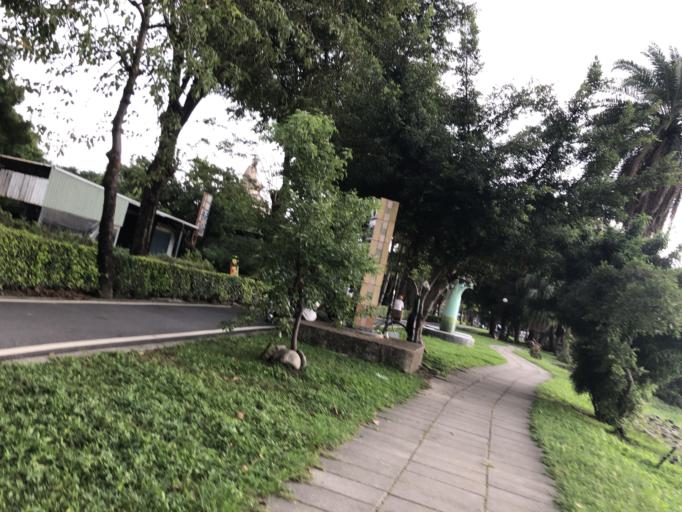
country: TW
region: Kaohsiung
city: Kaohsiung
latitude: 22.6856
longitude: 120.2997
